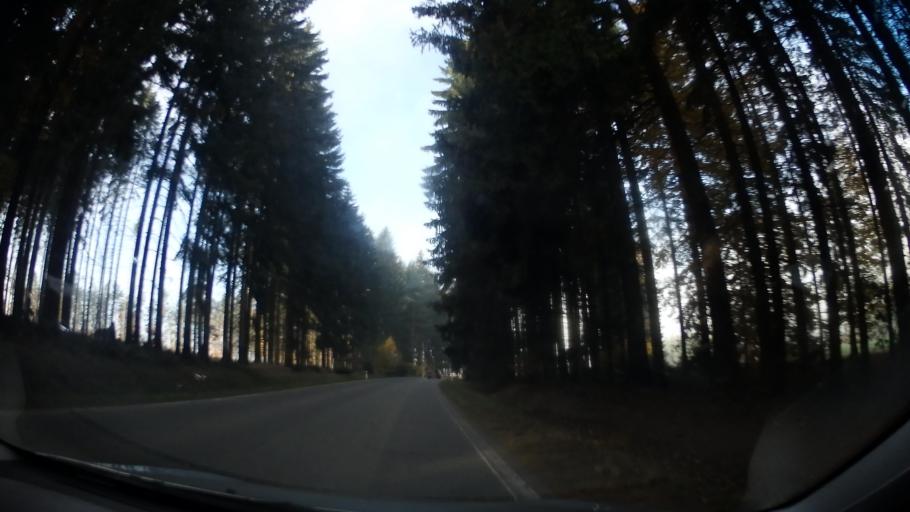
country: CZ
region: Vysocina
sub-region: Okres Zd'ar nad Sazavou
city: Nove Mesto na Morave
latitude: 49.4821
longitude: 16.0155
